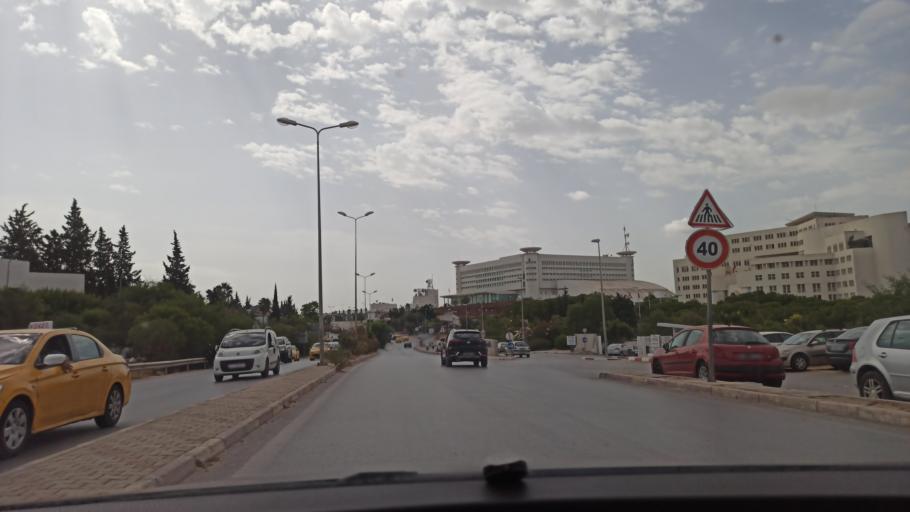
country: TN
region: Tunis
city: Tunis
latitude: 36.8322
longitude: 10.1567
